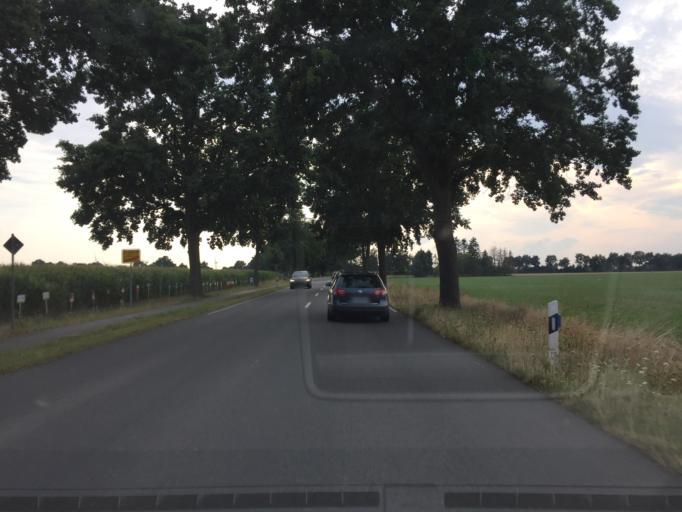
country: DE
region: Lower Saxony
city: Bohme
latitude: 52.8296
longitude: 9.4825
